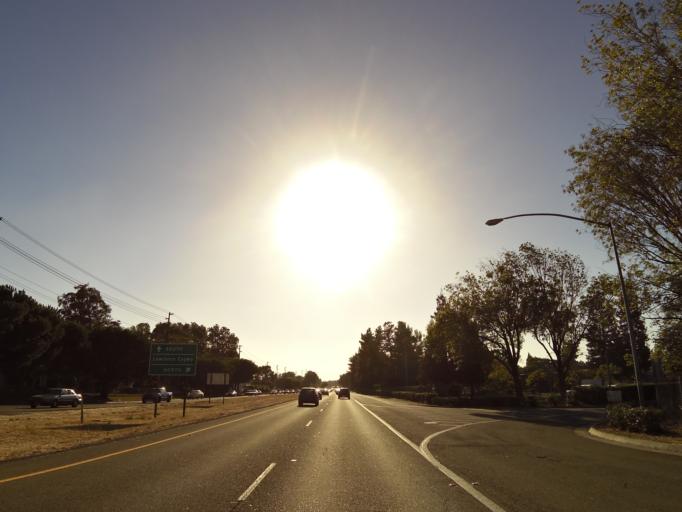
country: US
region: California
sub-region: Santa Clara County
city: Santa Clara
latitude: 37.3778
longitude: -121.9906
